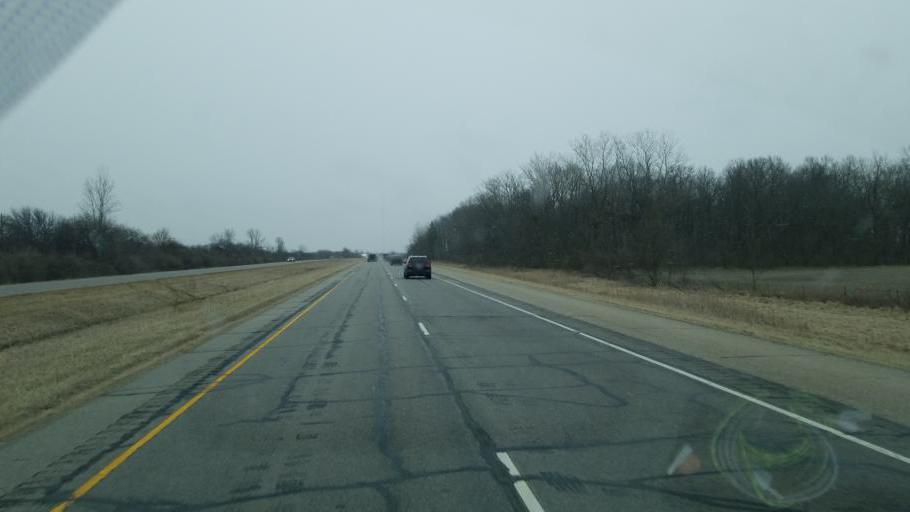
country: US
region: Indiana
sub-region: Miami County
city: Peru
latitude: 40.8082
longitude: -85.9531
